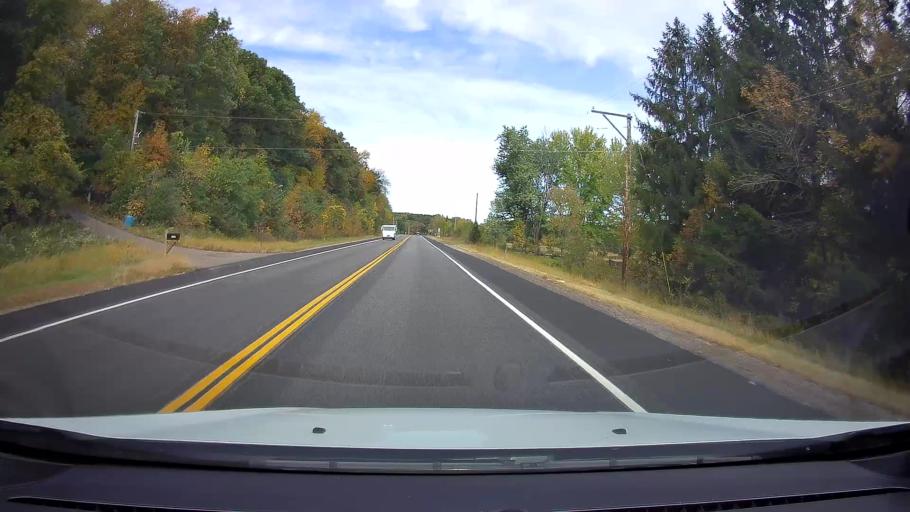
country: US
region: Wisconsin
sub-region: Saint Croix County
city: Somerset
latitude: 45.1403
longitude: -92.7585
